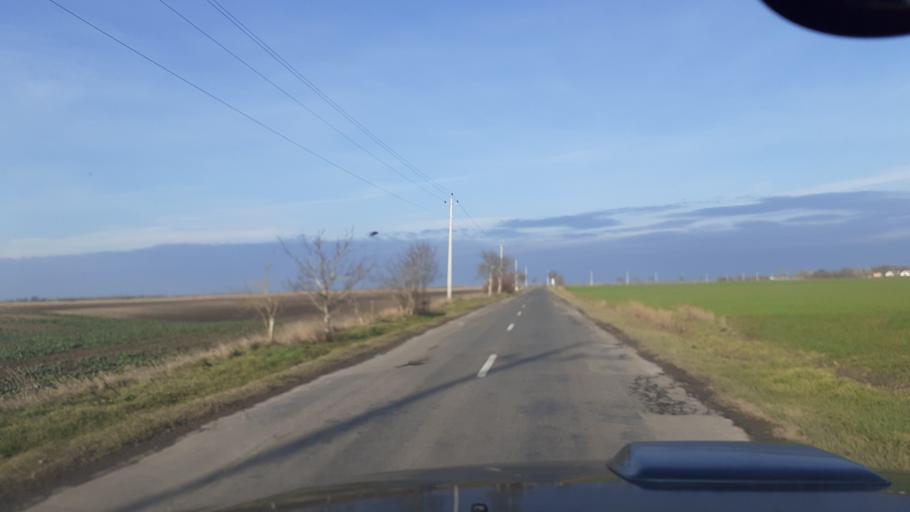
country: HU
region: Pest
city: Domsod
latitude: 47.0971
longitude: 19.0466
